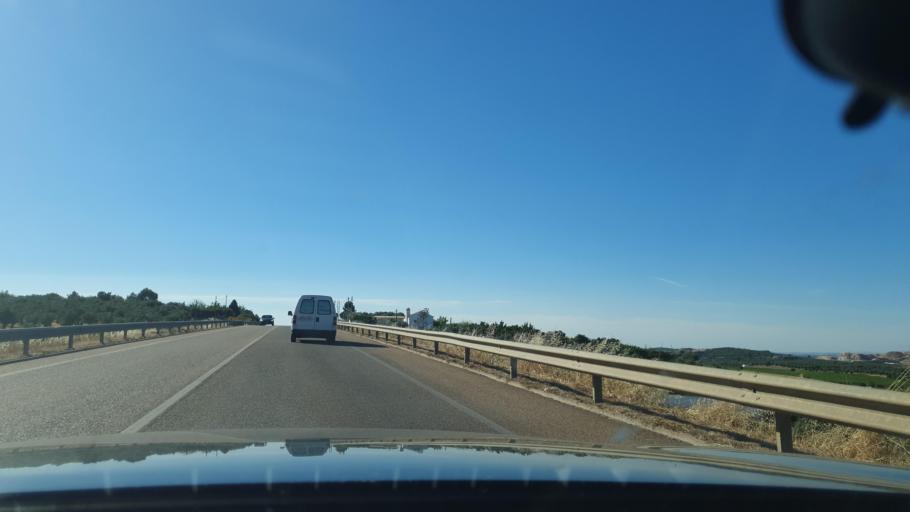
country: PT
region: Evora
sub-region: Vila Vicosa
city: Vila Vicosa
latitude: 38.7742
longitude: -7.4358
